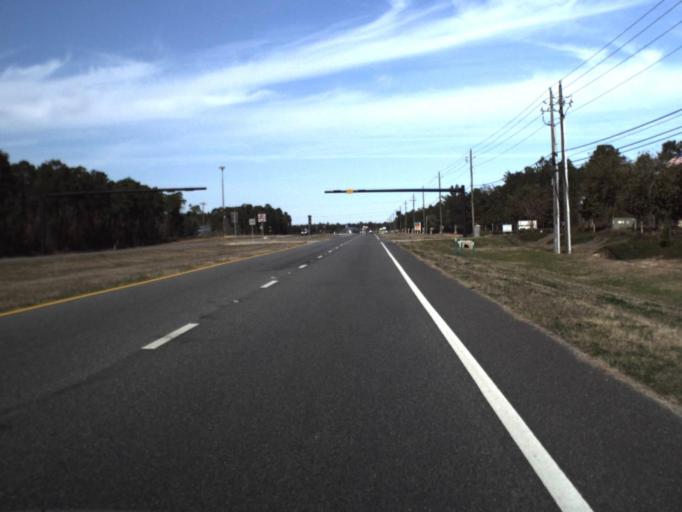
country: US
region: Florida
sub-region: Bay County
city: Lynn Haven
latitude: 30.3853
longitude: -85.6843
